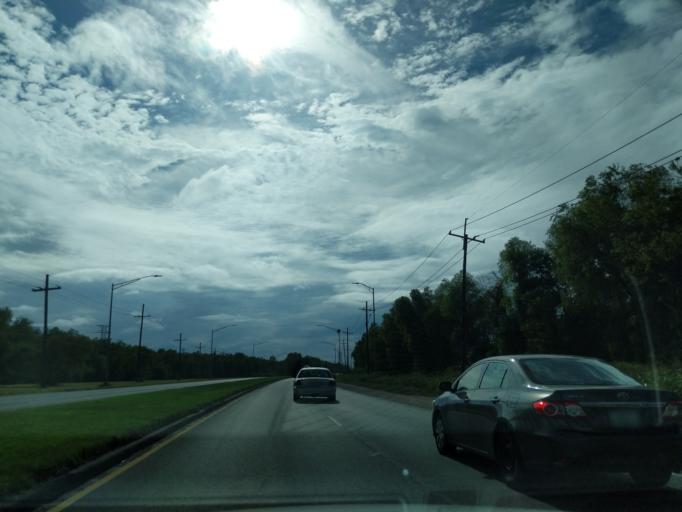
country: US
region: Louisiana
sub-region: Saint Bernard Parish
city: Chalmette
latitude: 30.0412
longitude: -89.8976
